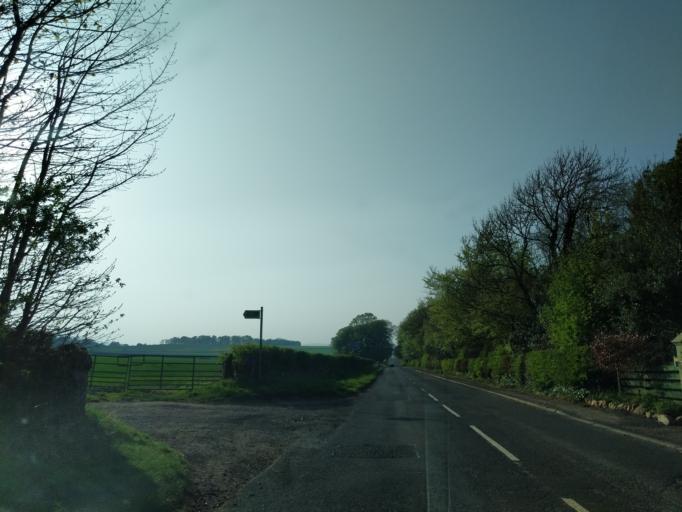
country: GB
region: Scotland
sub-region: Fife
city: Pathhead
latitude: 55.8771
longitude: -3.0071
